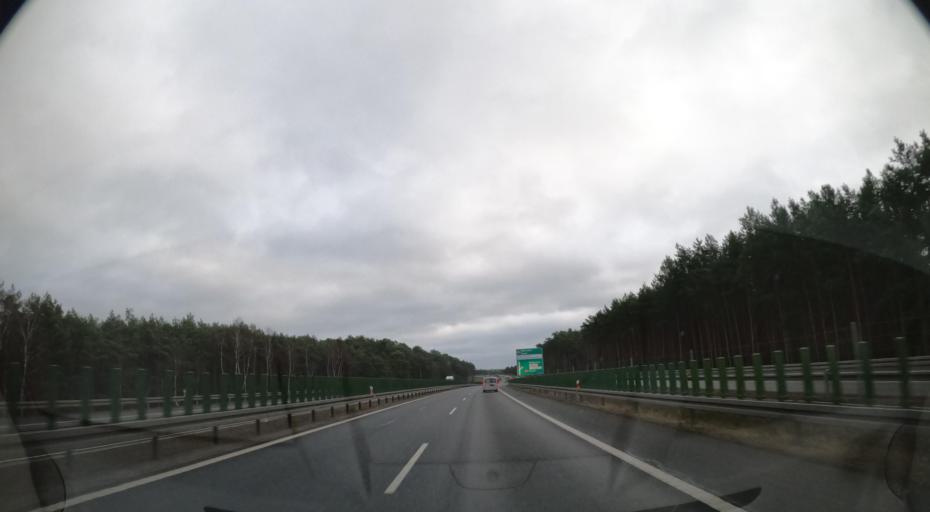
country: PL
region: Kujawsko-Pomorskie
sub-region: Bydgoszcz
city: Bydgoszcz
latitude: 53.0549
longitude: 17.9805
